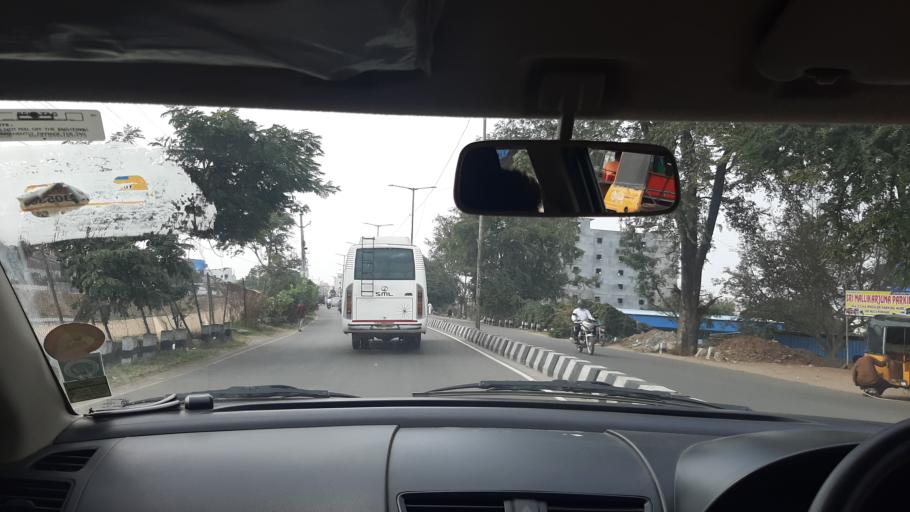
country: IN
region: Telangana
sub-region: Rangareddi
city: Lal Bahadur Nagar
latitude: 17.3429
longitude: 78.5448
